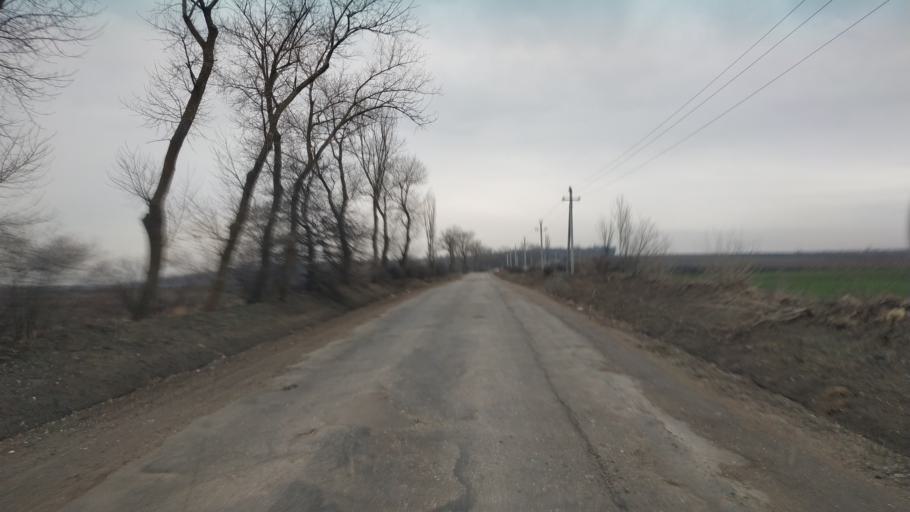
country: MD
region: Chisinau
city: Singera
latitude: 46.8508
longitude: 29.0015
